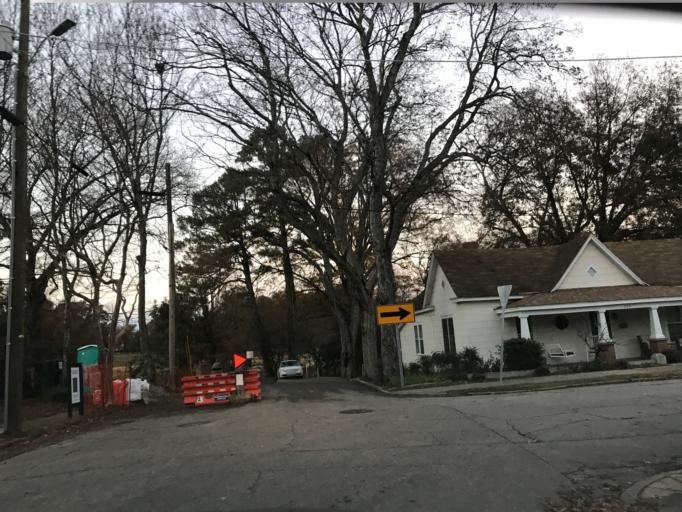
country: US
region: North Carolina
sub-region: Wake County
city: West Raleigh
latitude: 35.7912
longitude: -78.6487
